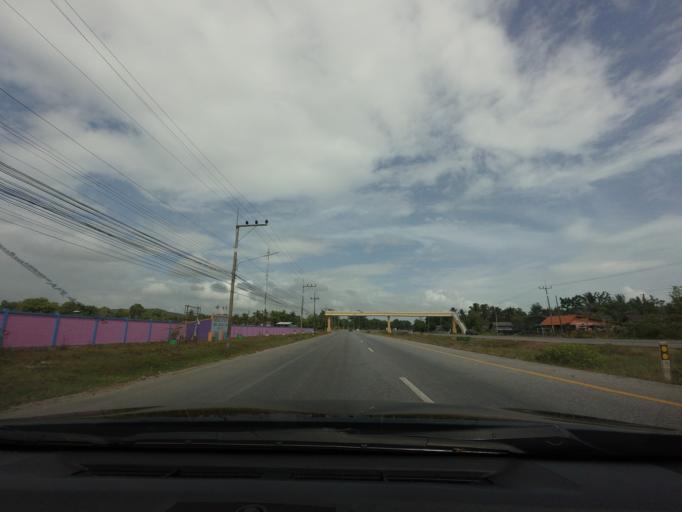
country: TH
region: Songkhla
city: Thepha
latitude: 6.9012
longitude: 100.9100
